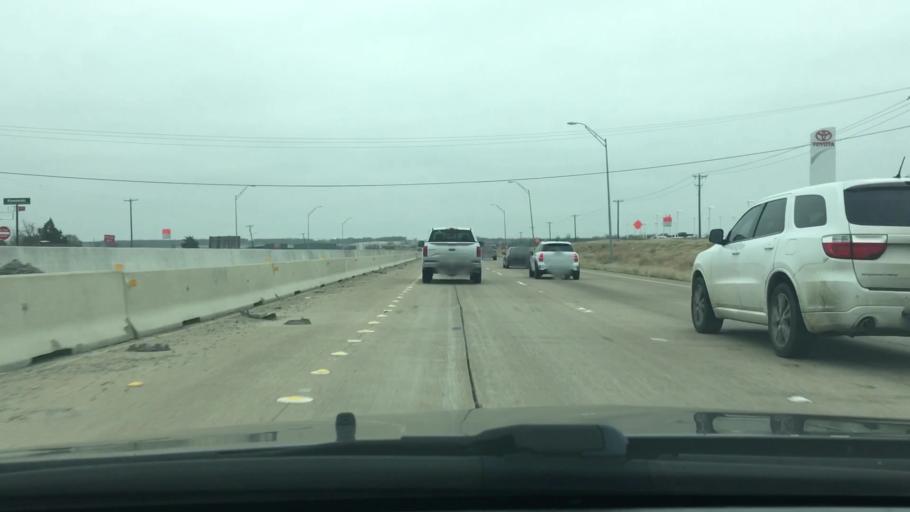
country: US
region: Texas
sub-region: Navarro County
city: Corsicana
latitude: 32.0579
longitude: -96.4515
